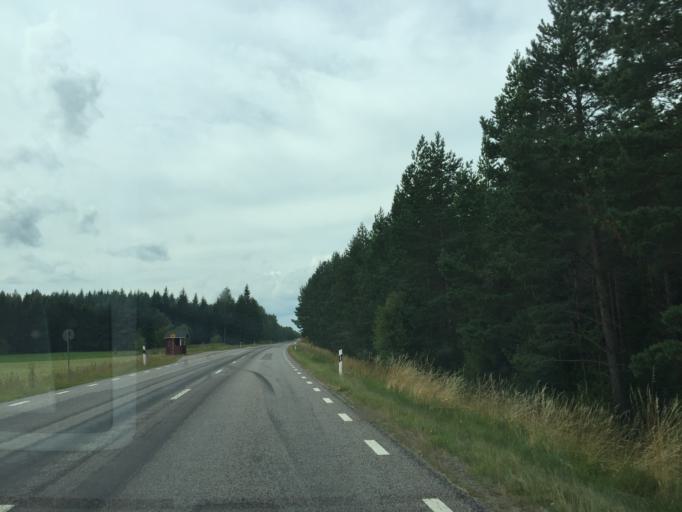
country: SE
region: Uppsala
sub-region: Tierps Kommun
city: Tierp
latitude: 60.3596
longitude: 17.3700
